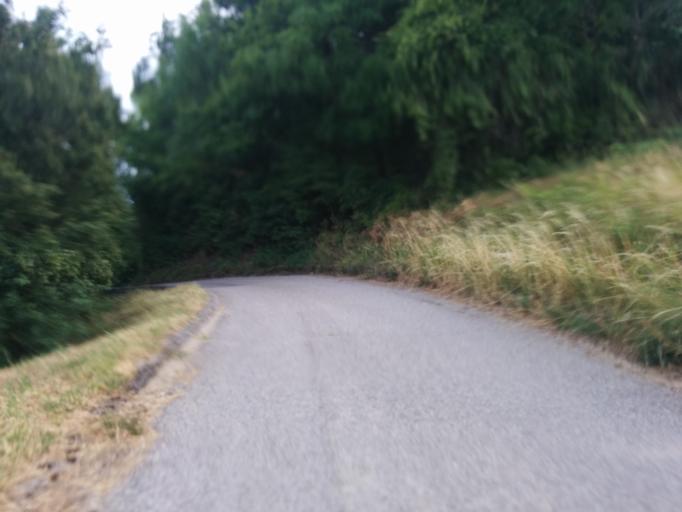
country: AT
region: Lower Austria
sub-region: Politischer Bezirk Modling
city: Gumpoldskirchen
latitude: 48.0379
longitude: 16.2621
